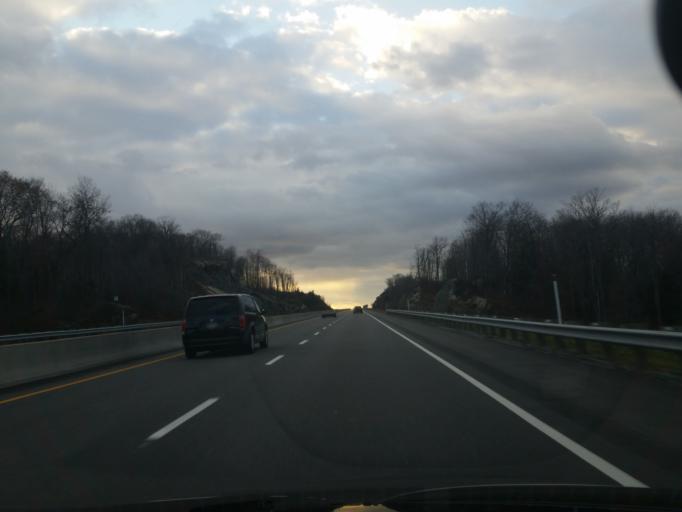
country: CA
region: Quebec
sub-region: Outaouais
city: Papineauville
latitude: 45.6688
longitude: -74.9832
